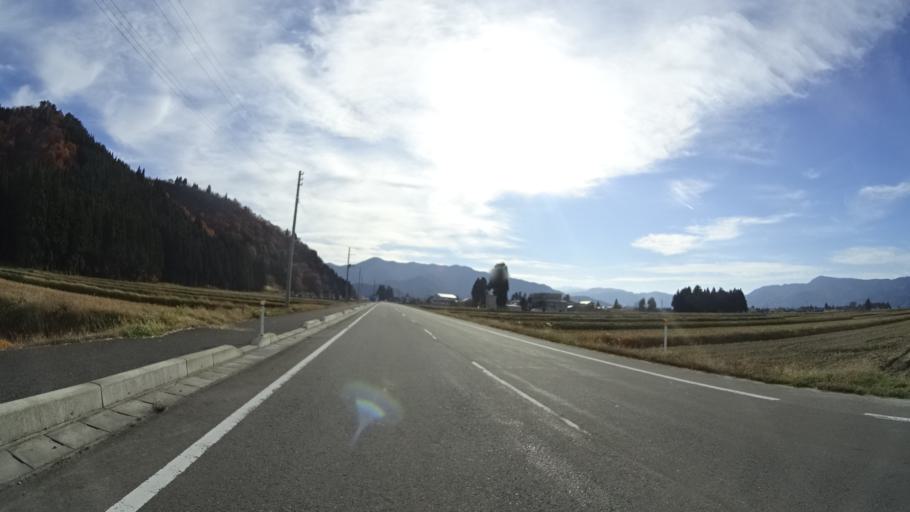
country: JP
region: Niigata
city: Shiozawa
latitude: 37.0291
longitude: 138.8831
